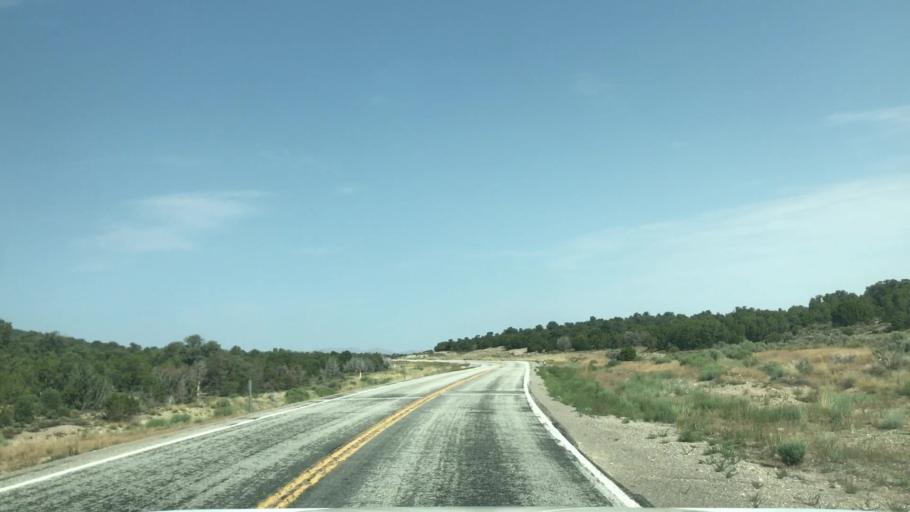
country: US
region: Nevada
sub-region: White Pine County
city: McGill
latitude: 39.1356
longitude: -114.3274
